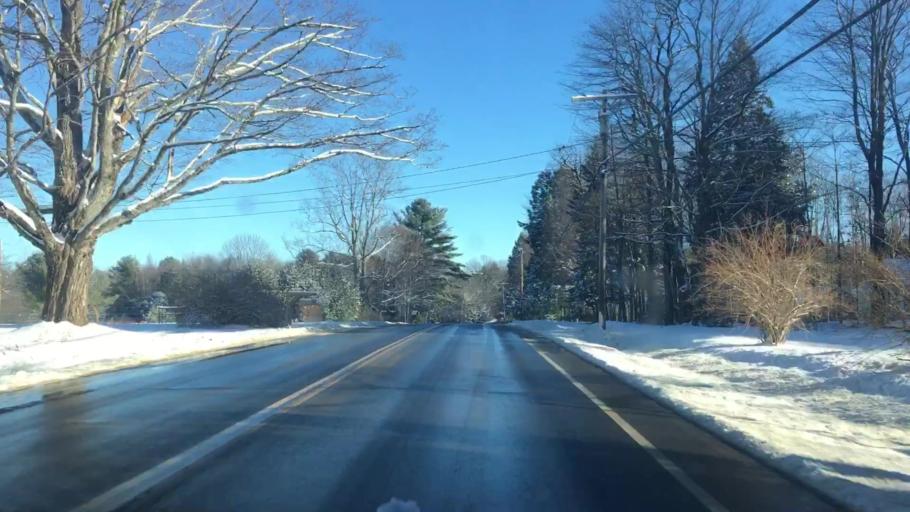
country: US
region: Maine
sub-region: Sagadahoc County
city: Topsham
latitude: 43.9137
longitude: -70.0229
